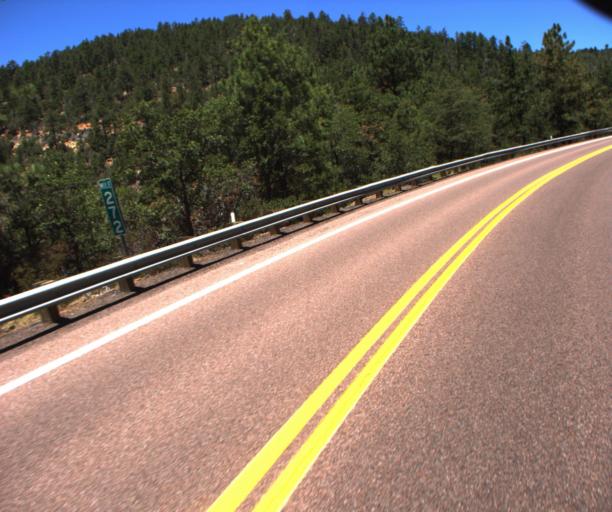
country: US
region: Arizona
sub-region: Gila County
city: Pine
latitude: 34.4187
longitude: -111.5012
